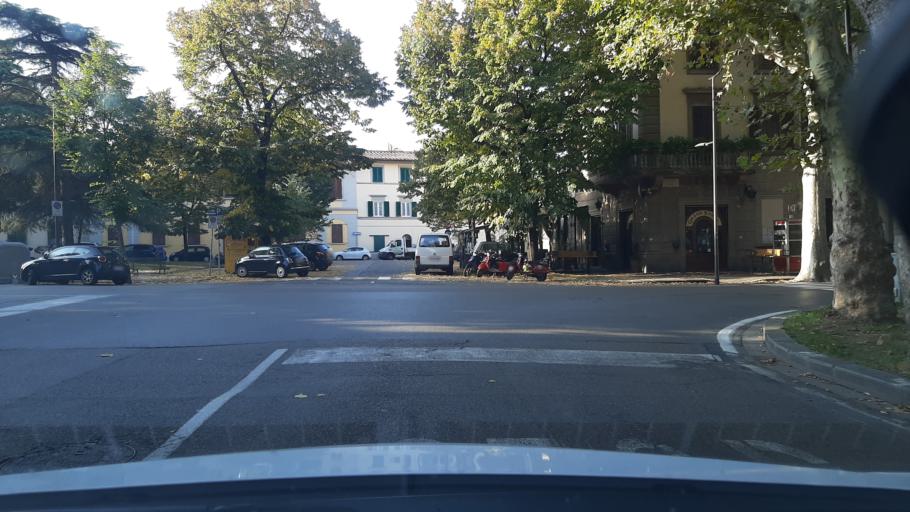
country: IT
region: Tuscany
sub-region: Province of Florence
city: Fiesole
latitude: 43.7749
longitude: 11.2845
